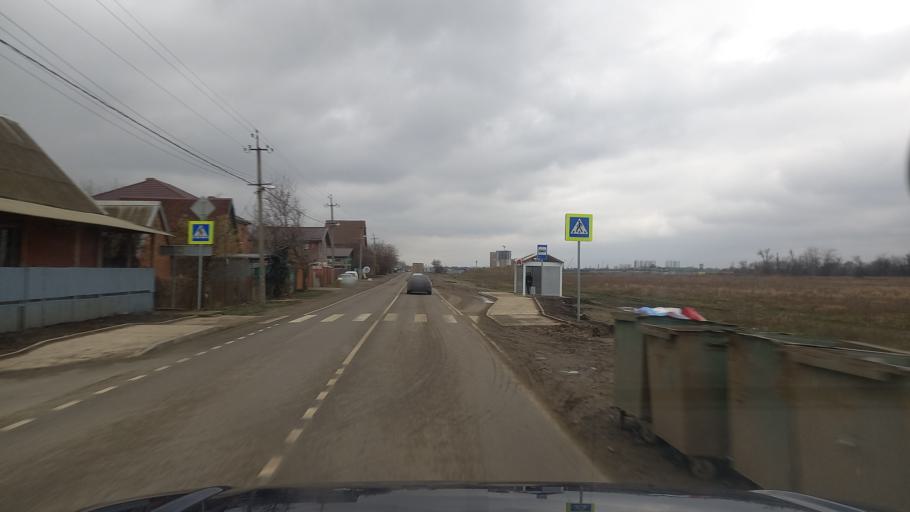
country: RU
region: Krasnodarskiy
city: Pashkovskiy
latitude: 45.0593
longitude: 39.1653
